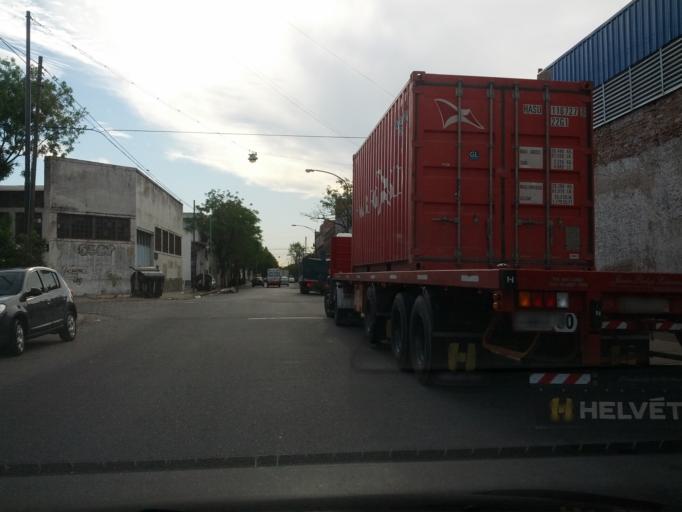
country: AR
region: Buenos Aires
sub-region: Partido de Avellaneda
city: Avellaneda
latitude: -34.6478
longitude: -58.4044
